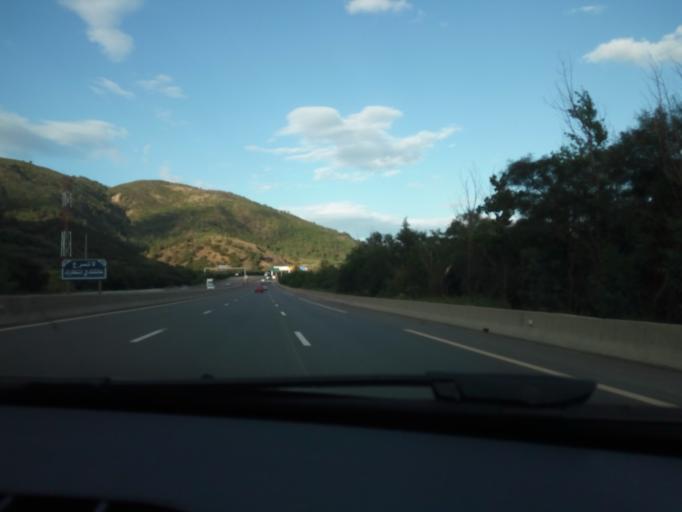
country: DZ
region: Tipaza
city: El Affroun
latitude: 36.3907
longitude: 2.5018
